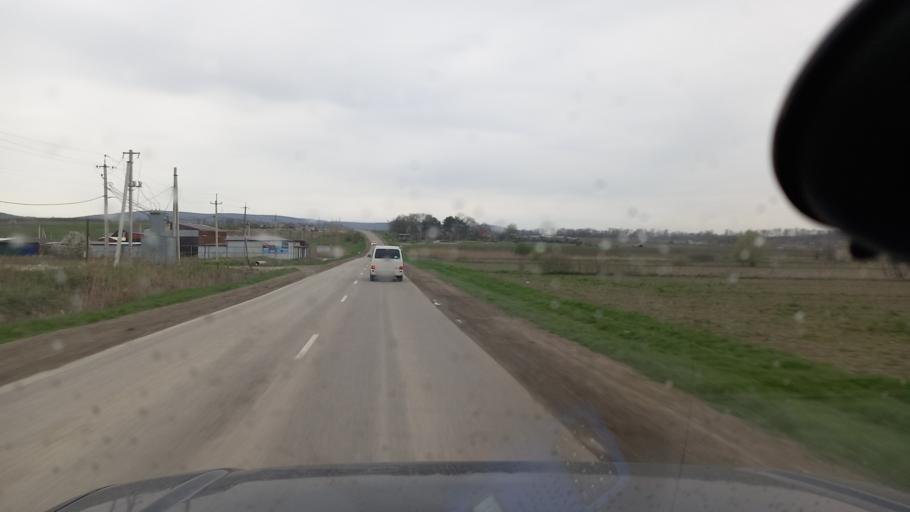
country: RU
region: Krasnodarskiy
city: Anapskaya
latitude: 44.8878
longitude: 37.4570
